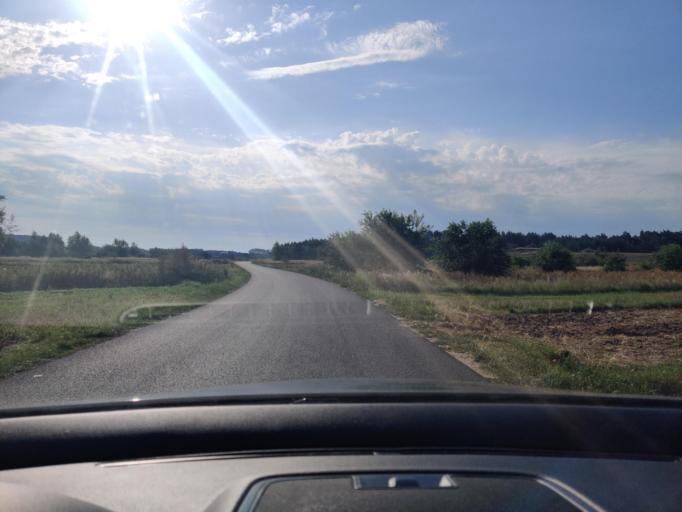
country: PL
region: Greater Poland Voivodeship
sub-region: Konin
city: Konin
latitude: 52.1868
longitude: 18.3247
